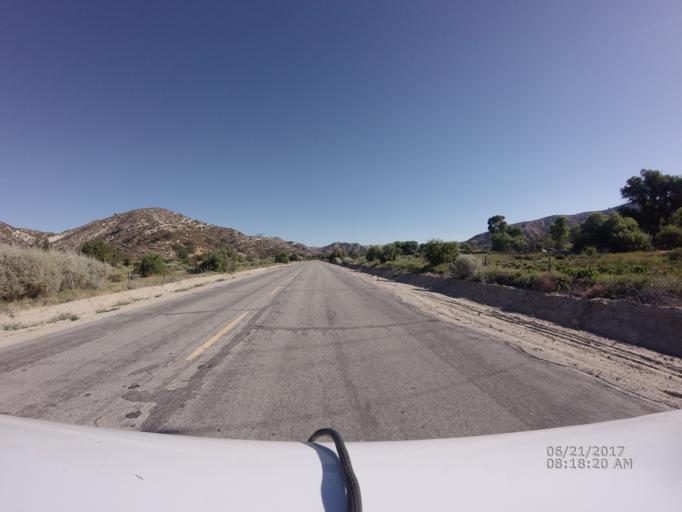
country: US
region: California
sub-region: Kern County
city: Lebec
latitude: 34.7163
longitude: -118.8018
